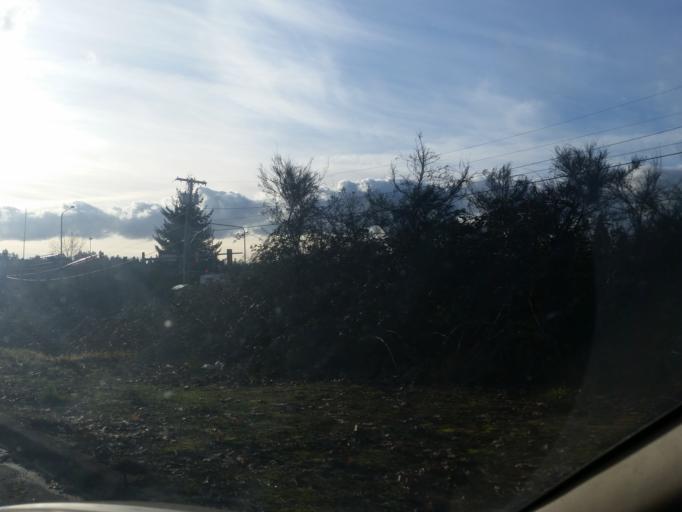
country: US
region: Washington
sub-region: King County
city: Woodinville
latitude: 47.7594
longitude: -122.1558
